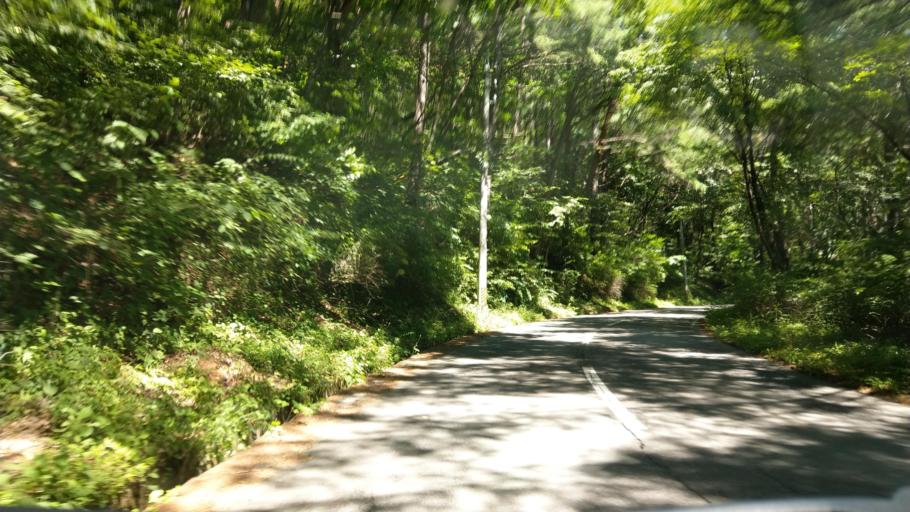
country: JP
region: Nagano
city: Komoro
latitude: 36.3697
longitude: 138.4607
